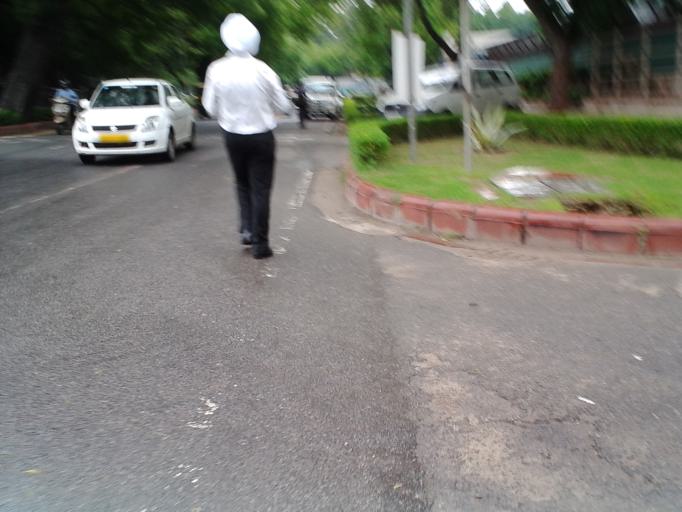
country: IN
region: NCT
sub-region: New Delhi
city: New Delhi
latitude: 28.6101
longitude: 77.2357
